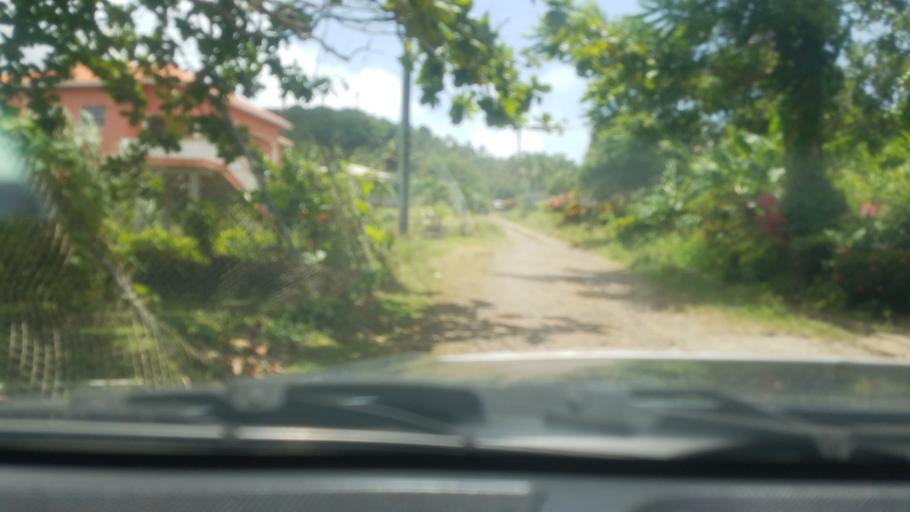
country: LC
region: Laborie Quarter
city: Laborie
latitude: 13.7728
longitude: -60.9513
